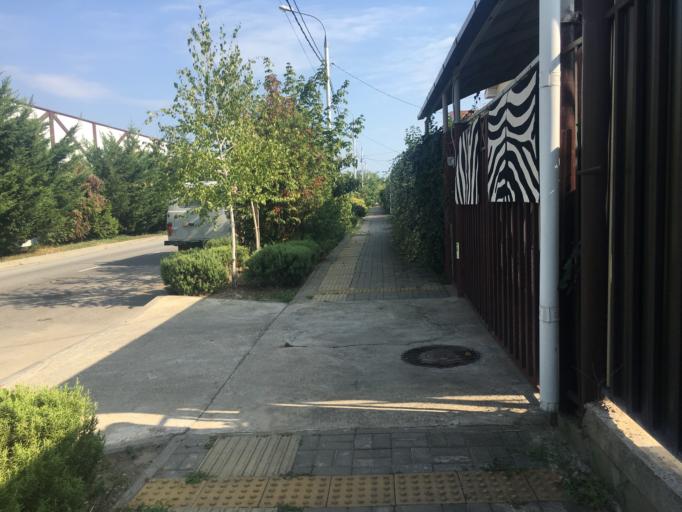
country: RU
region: Krasnodarskiy
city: Vysokoye
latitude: 43.3955
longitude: 40.0004
